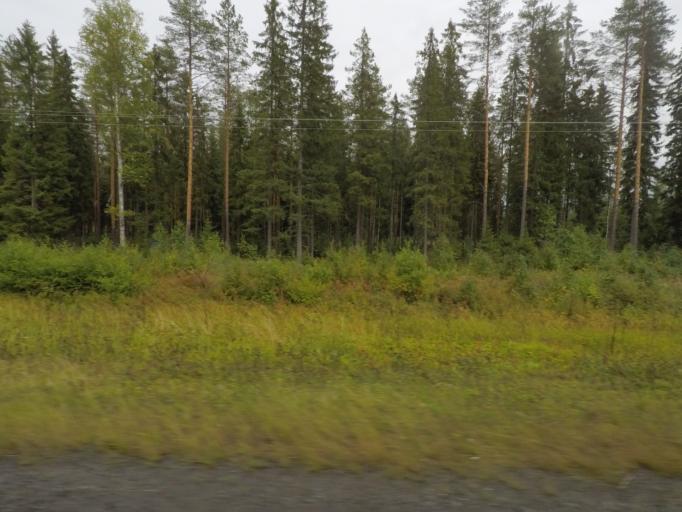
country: FI
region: Southern Savonia
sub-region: Pieksaemaeki
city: Juva
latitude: 61.9722
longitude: 27.8040
